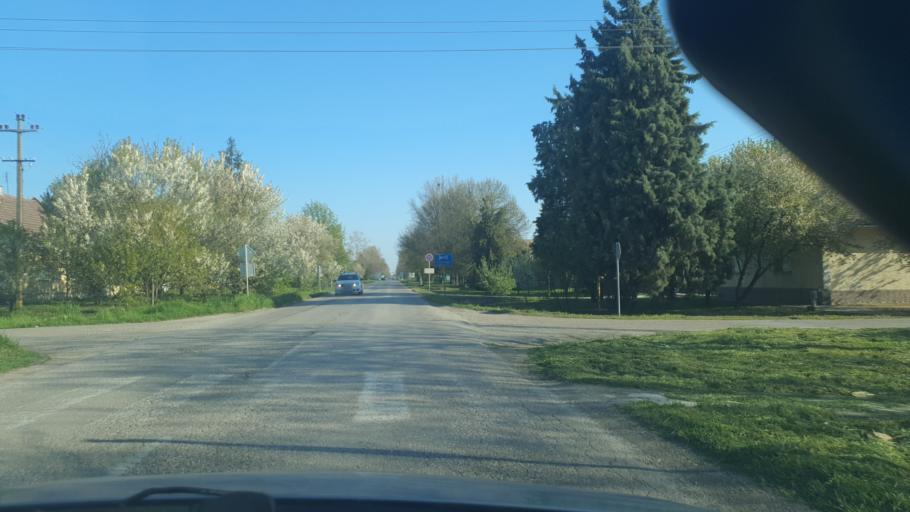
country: RS
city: Zmajevo
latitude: 45.4953
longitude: 19.6901
